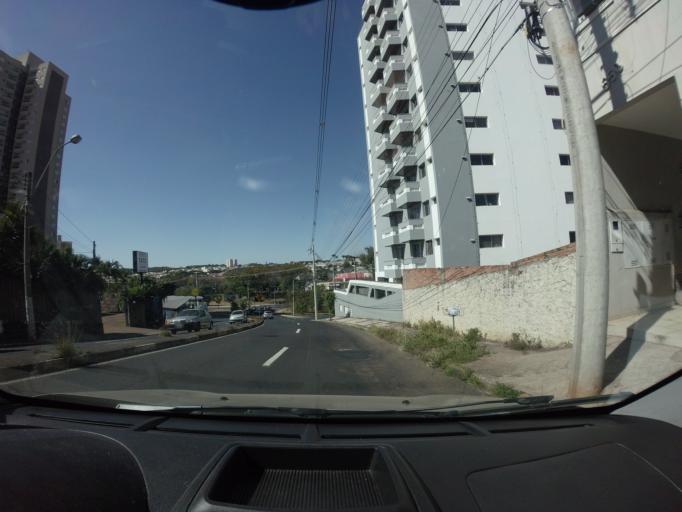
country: BR
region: Sao Paulo
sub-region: Piracicaba
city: Piracicaba
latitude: -22.7259
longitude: -47.6285
